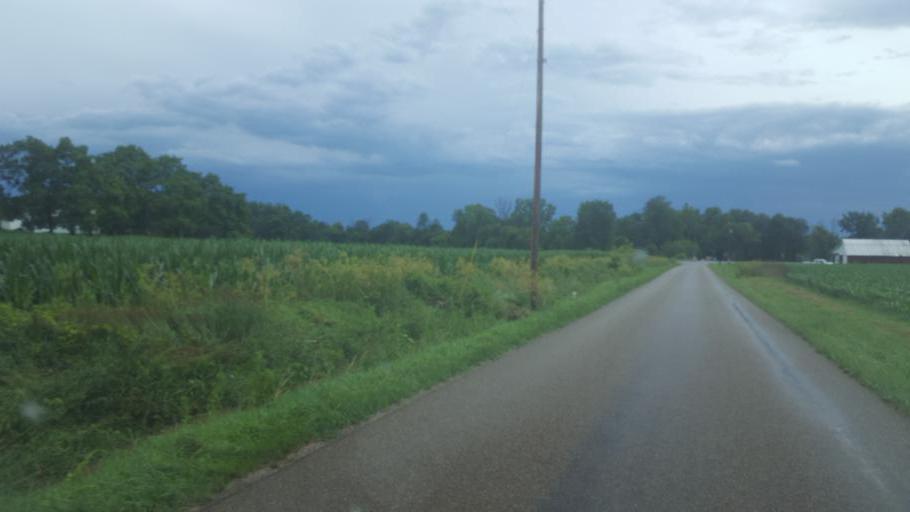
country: US
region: Ohio
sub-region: Knox County
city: Fredericktown
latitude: 40.4648
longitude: -82.6266
